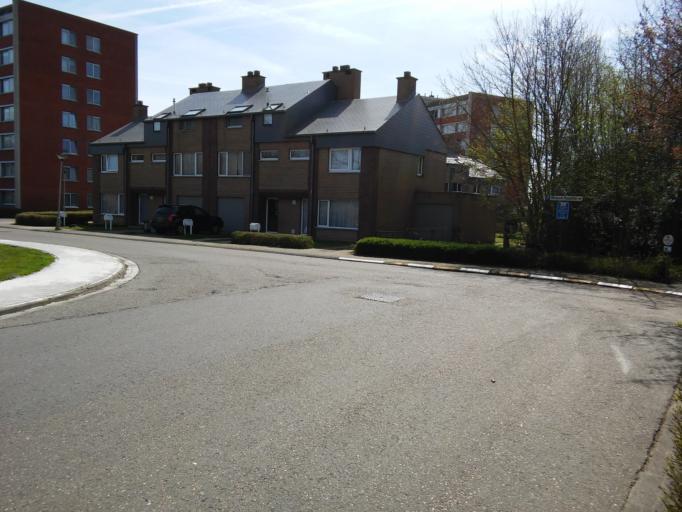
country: BE
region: Flanders
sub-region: Provincie Antwerpen
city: Rumst
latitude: 51.0787
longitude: 4.3954
